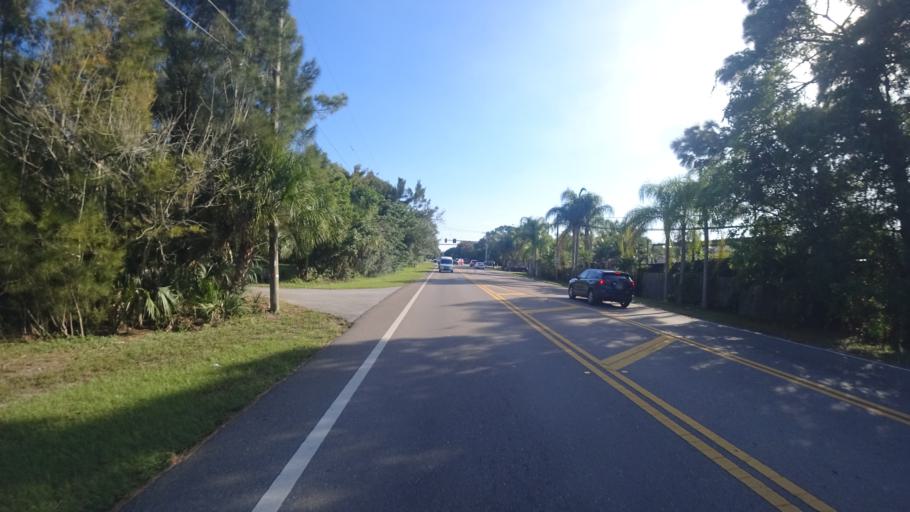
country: US
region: Florida
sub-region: Sarasota County
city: North Sarasota
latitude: 27.3826
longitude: -82.5139
